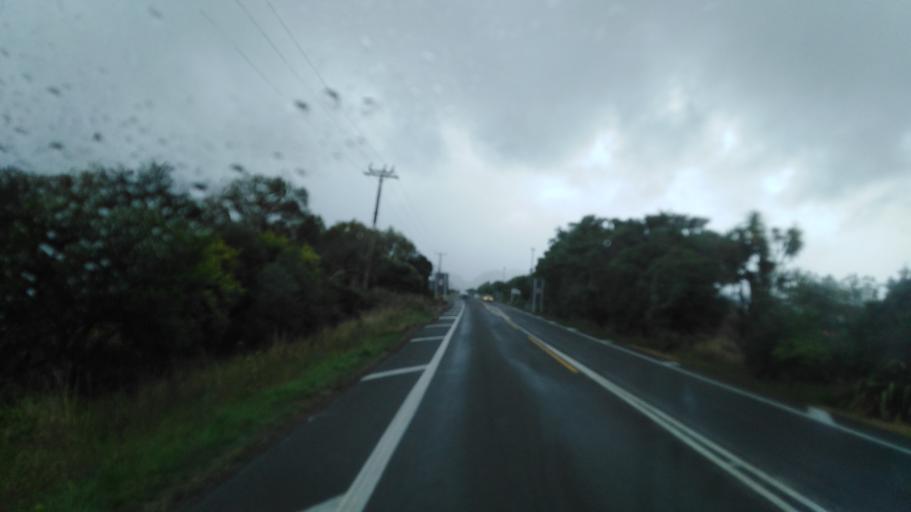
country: NZ
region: Marlborough
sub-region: Marlborough District
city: Blenheim
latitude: -41.4588
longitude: 173.9624
